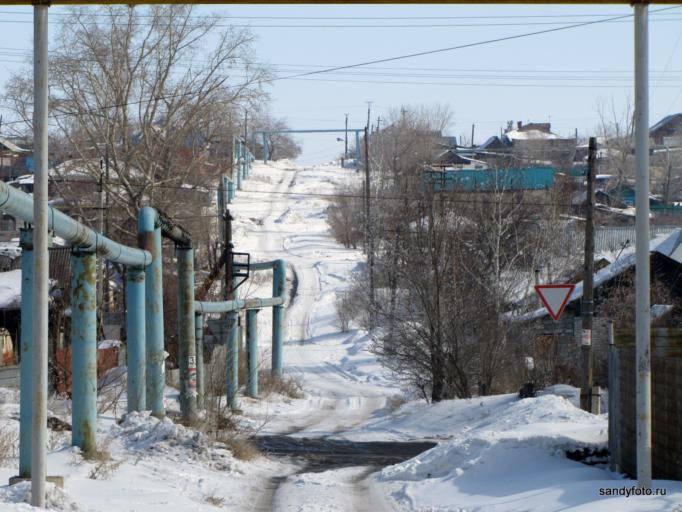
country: RU
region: Chelyabinsk
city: Troitsk
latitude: 54.1000
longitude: 61.5611
